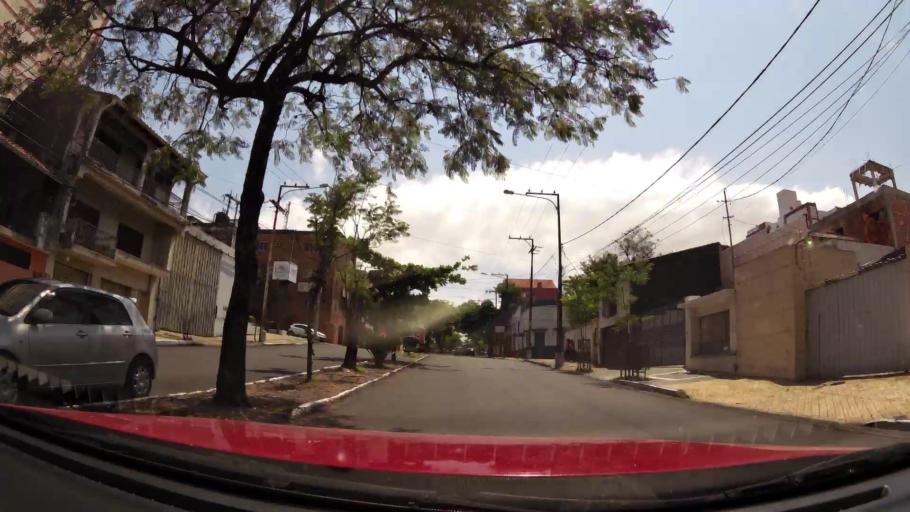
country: PY
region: Asuncion
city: Asuncion
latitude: -25.2882
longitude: -57.6438
